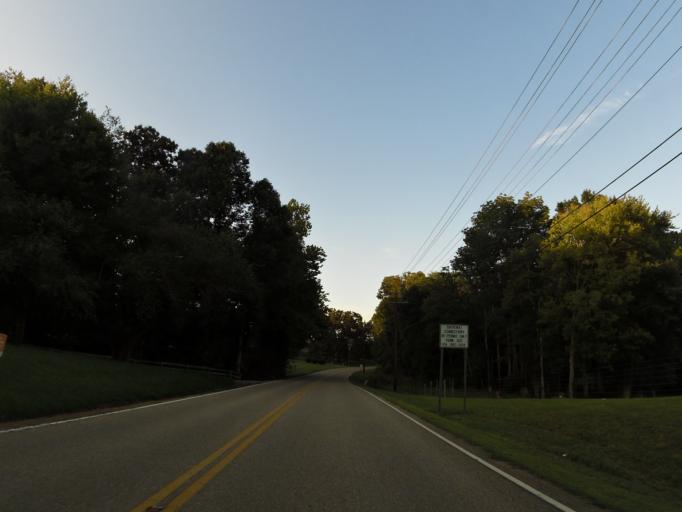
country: US
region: Tennessee
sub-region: Roane County
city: Rockwood
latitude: 35.7264
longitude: -84.6334
